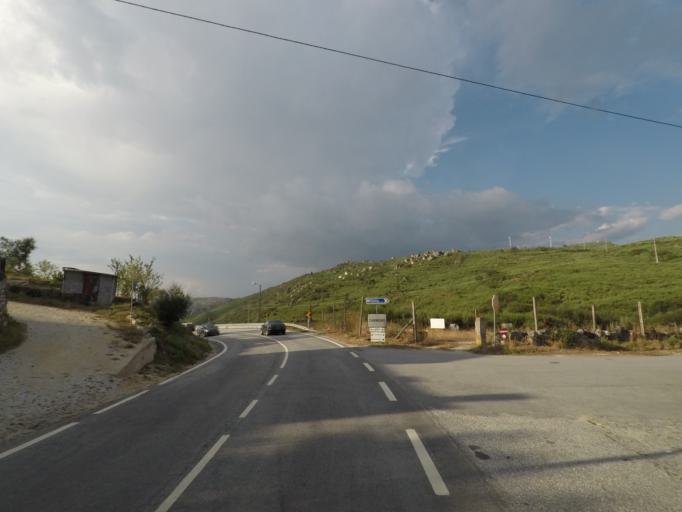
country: PT
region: Porto
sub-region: Baiao
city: Valadares
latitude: 41.1966
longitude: -7.9475
